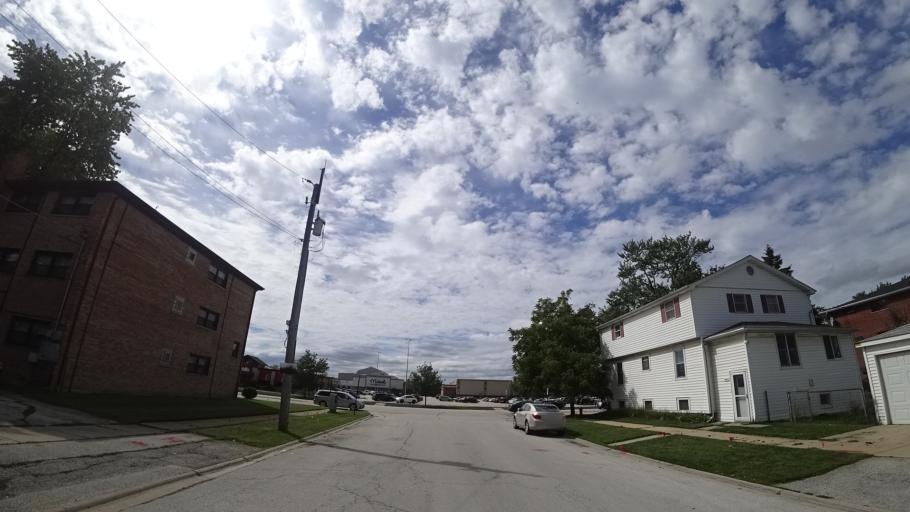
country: US
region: Illinois
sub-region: Cook County
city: Chicago Ridge
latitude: 41.7159
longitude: -87.7792
